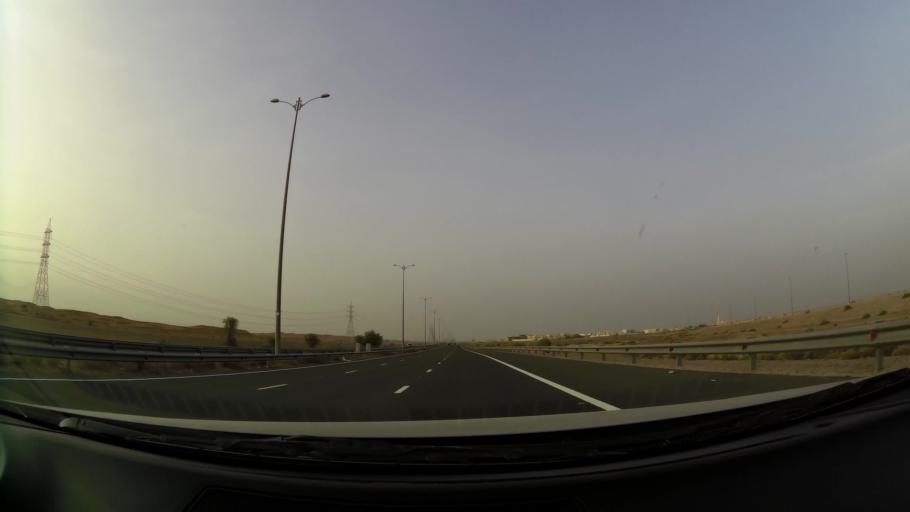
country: OM
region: Al Buraimi
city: Al Buraymi
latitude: 24.3403
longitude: 55.7736
